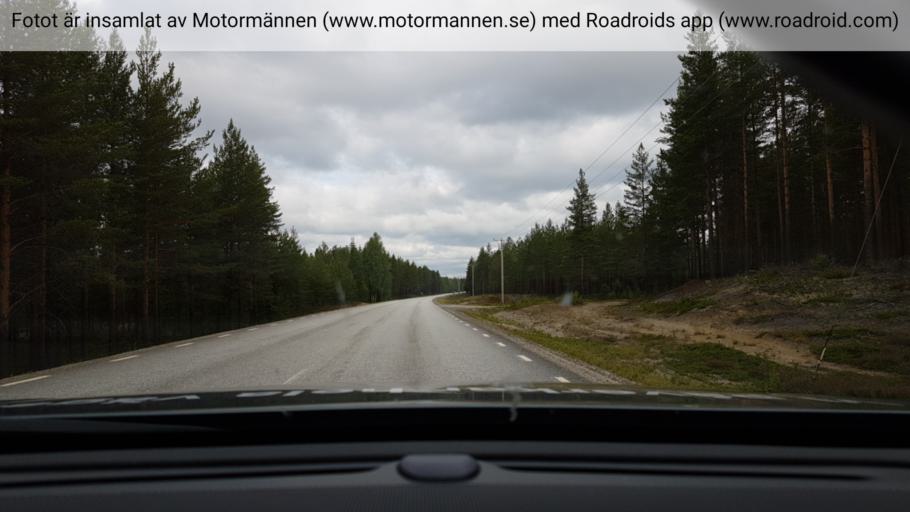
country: SE
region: Vaesterbotten
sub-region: Vindelns Kommun
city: Vindeln
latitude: 64.3221
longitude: 19.5456
